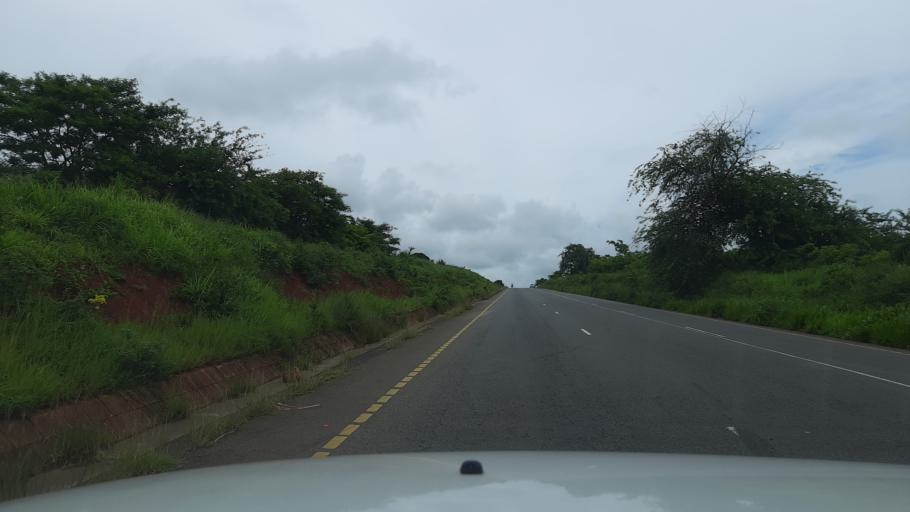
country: TZ
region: Pwani
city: Lugoba
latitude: -6.0387
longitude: 38.2402
